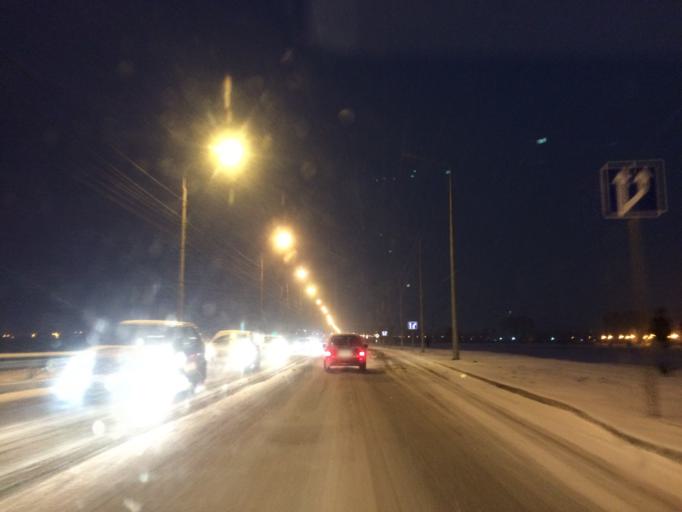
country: RU
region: Tula
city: Tula
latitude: 54.1896
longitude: 37.6560
